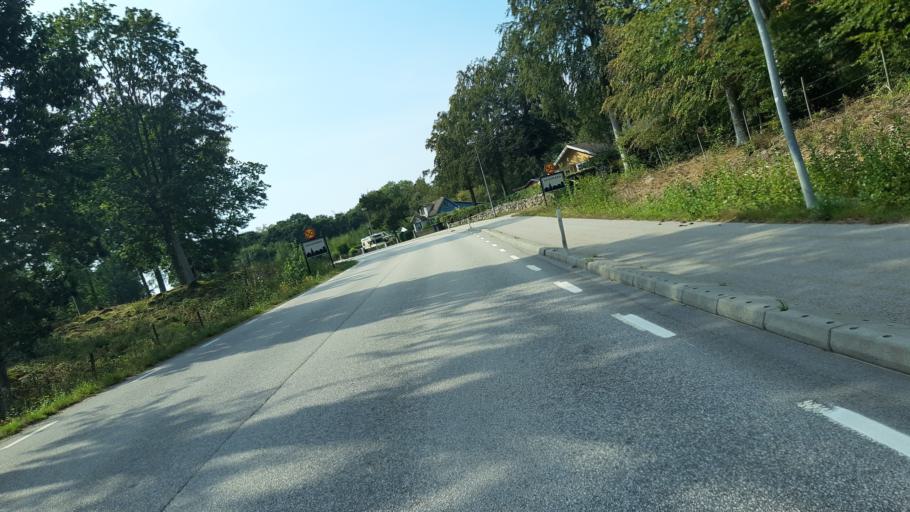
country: SE
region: Blekinge
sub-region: Ronneby Kommun
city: Ronneby
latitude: 56.1703
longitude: 15.2370
